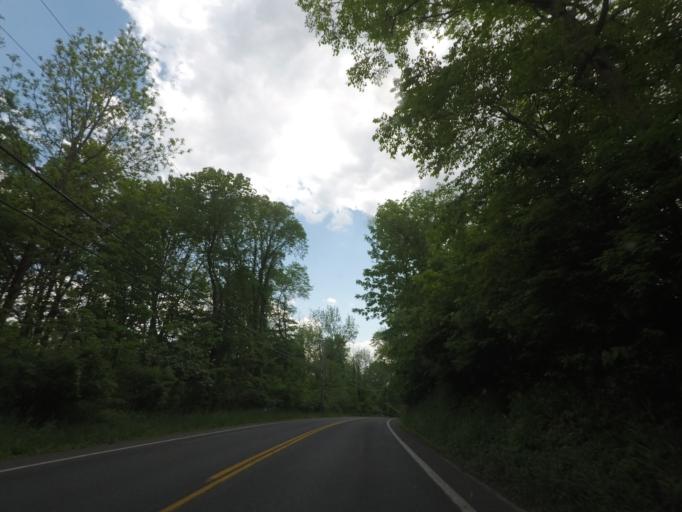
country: US
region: New York
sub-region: Dutchess County
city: Dover Plains
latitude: 41.8700
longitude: -73.5405
